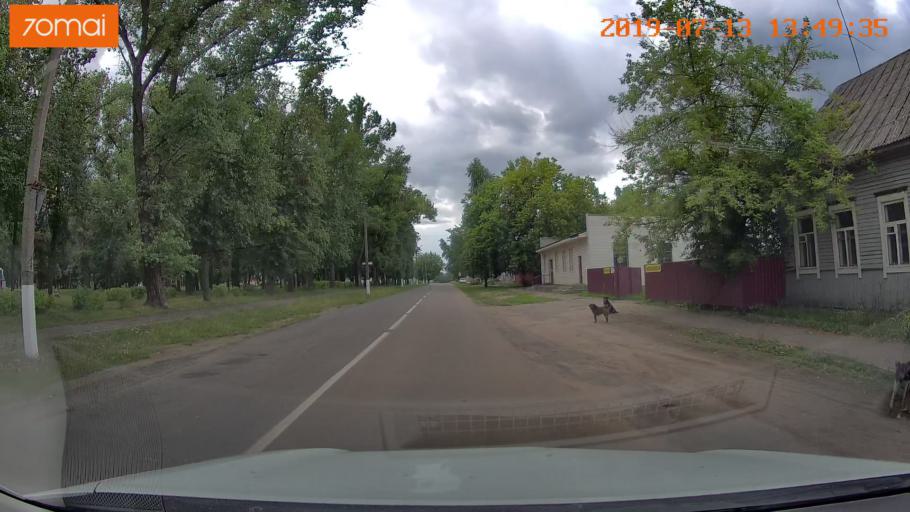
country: BY
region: Mogilev
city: Asipovichy
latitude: 53.2998
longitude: 28.6398
